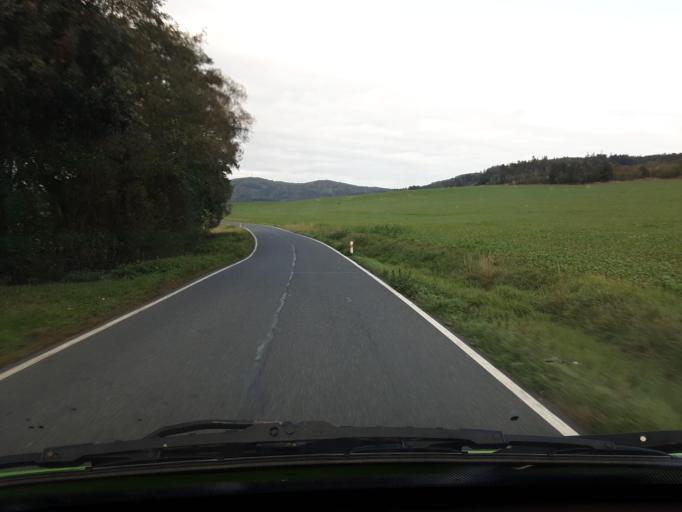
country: CZ
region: Plzensky
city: Janovice nad Uhlavou
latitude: 49.4063
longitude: 13.1565
